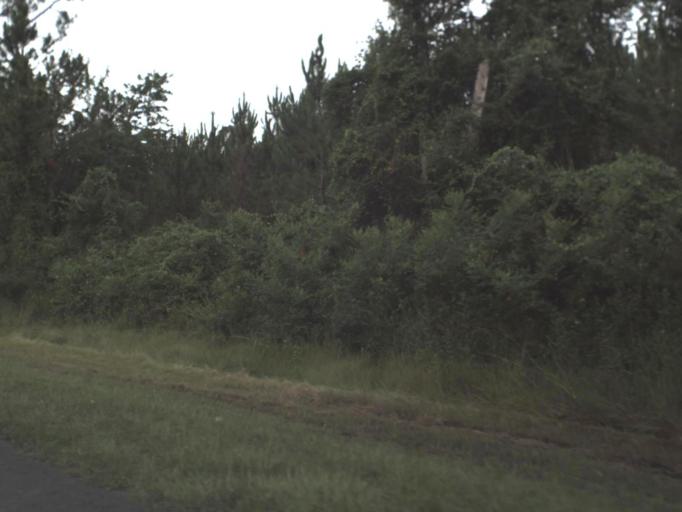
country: US
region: Florida
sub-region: Columbia County
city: Five Points
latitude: 30.3327
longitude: -82.6260
